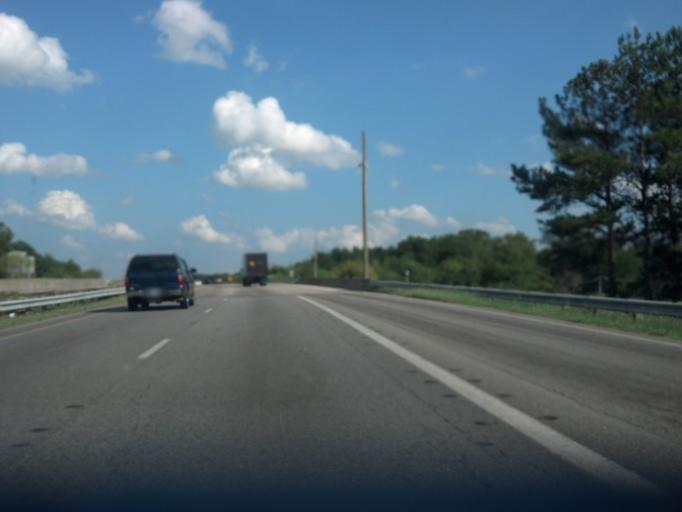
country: US
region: North Carolina
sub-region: Nash County
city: Rocky Mount
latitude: 35.9596
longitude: -77.7912
